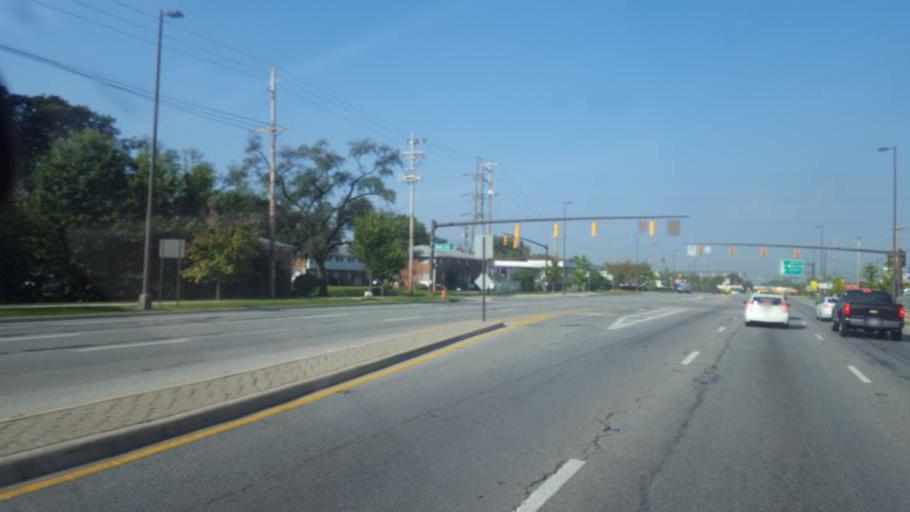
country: US
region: Ohio
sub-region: Franklin County
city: Worthington
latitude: 40.0615
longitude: -82.9917
